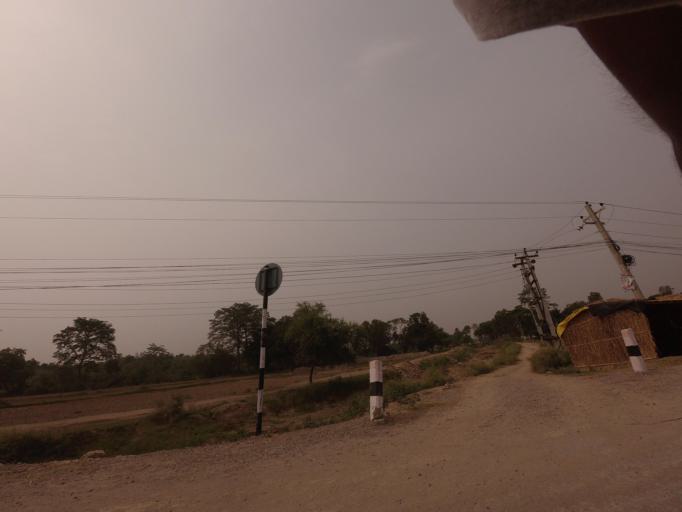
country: NP
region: Western Region
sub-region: Lumbini Zone
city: Bhairahawa
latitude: 27.5040
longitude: 83.3797
